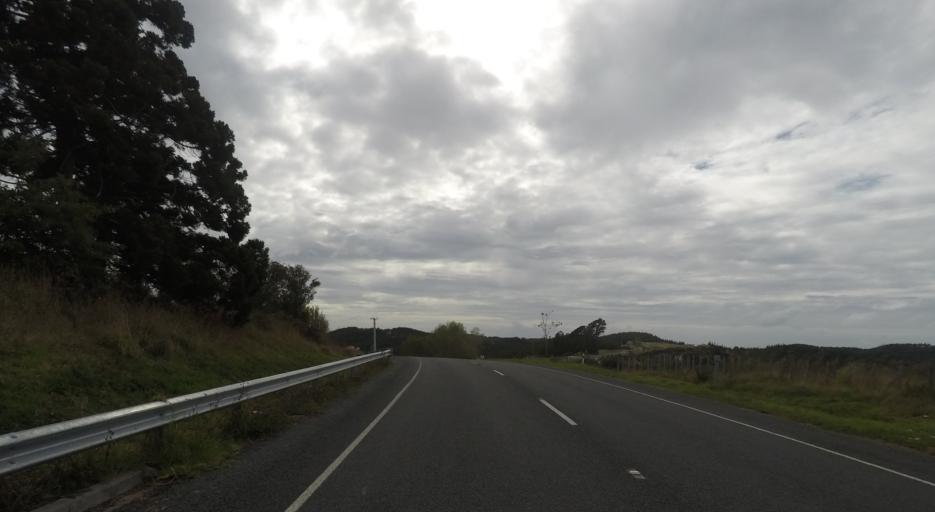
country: NZ
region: Auckland
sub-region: Auckland
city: Rothesay Bay
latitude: -36.6549
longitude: 174.6885
